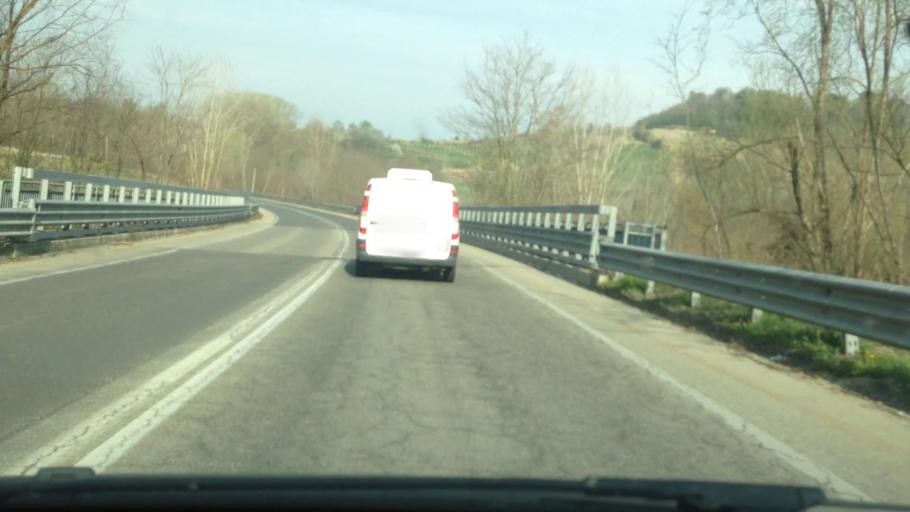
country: IT
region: Piedmont
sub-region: Provincia di Cuneo
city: Canale
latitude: 44.8048
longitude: 7.9745
